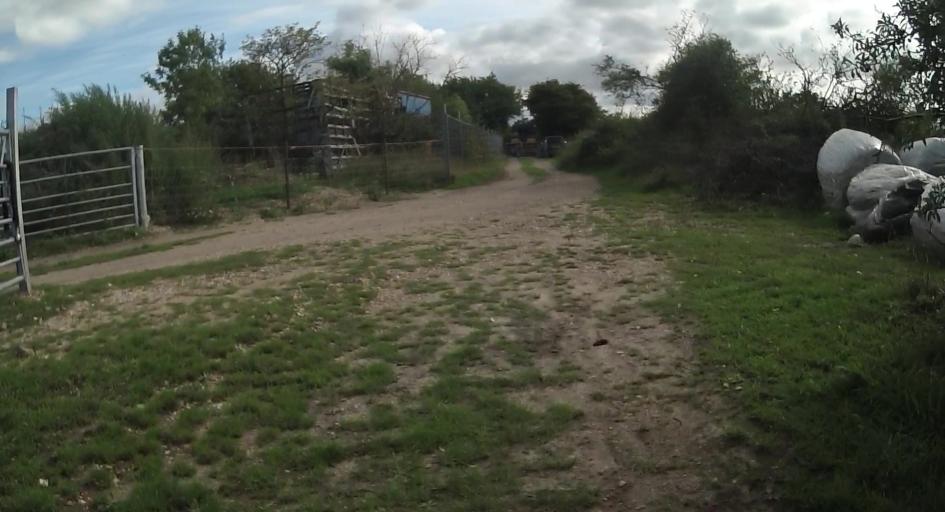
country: GB
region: England
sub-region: West Berkshire
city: Thatcham
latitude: 51.3808
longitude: -1.2403
